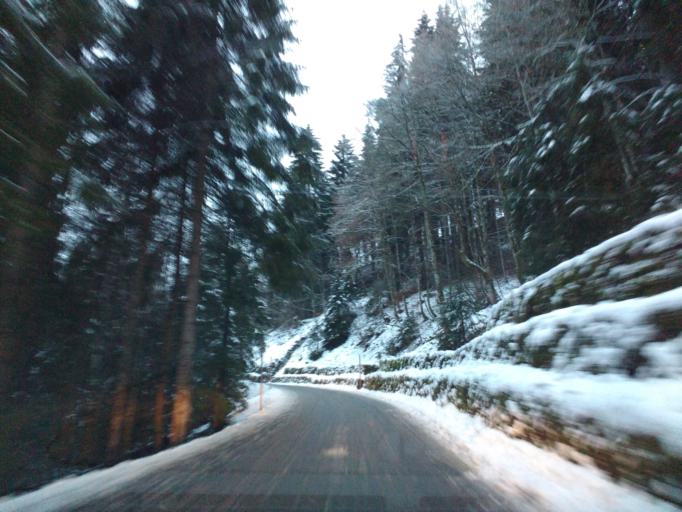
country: DE
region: Bavaria
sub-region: Swabia
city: Obermaiselstein
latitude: 47.4043
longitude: 10.2200
